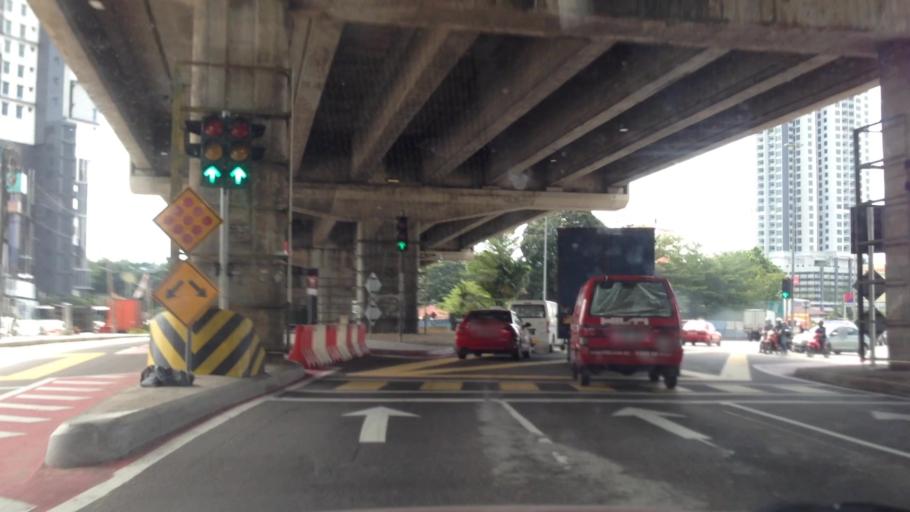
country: MY
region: Selangor
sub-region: Petaling
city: Petaling Jaya
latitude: 3.0836
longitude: 101.6617
